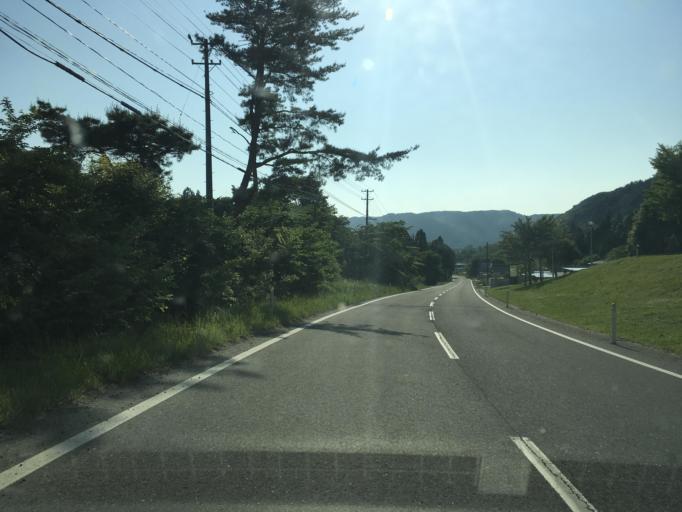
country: JP
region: Iwate
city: Ofunato
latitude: 39.1238
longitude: 141.7468
